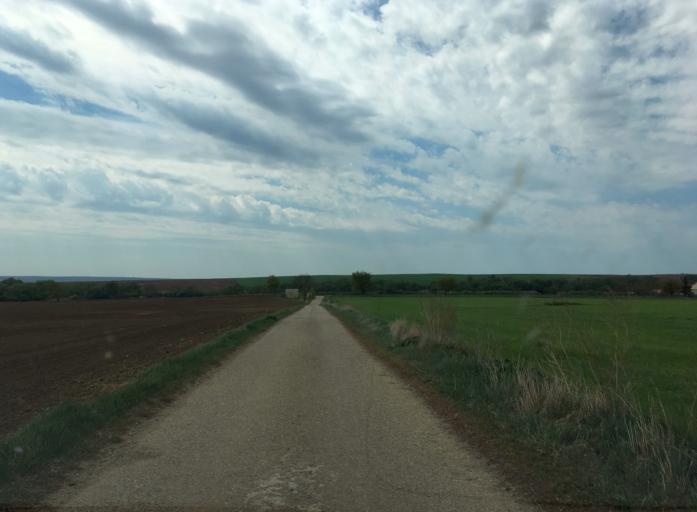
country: SK
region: Nitriansky
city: Svodin
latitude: 47.9176
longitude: 18.4100
